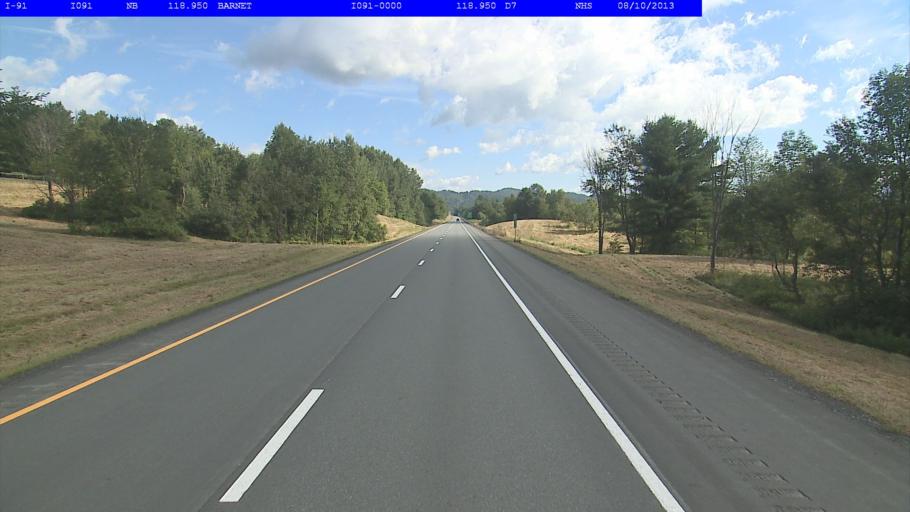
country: US
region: New Hampshire
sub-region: Grafton County
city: Woodsville
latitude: 44.2789
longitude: -72.0697
